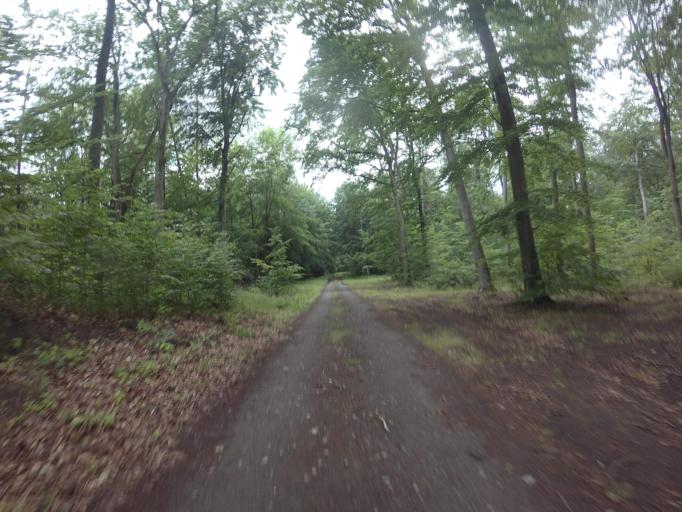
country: PL
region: West Pomeranian Voivodeship
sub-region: Powiat choszczenski
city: Bierzwnik
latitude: 53.0376
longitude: 15.5779
